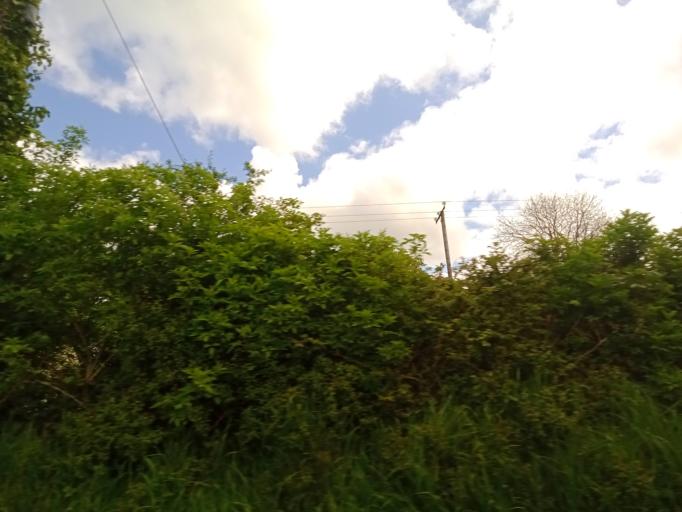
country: IE
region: Munster
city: Thurles
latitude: 52.6722
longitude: -7.6760
